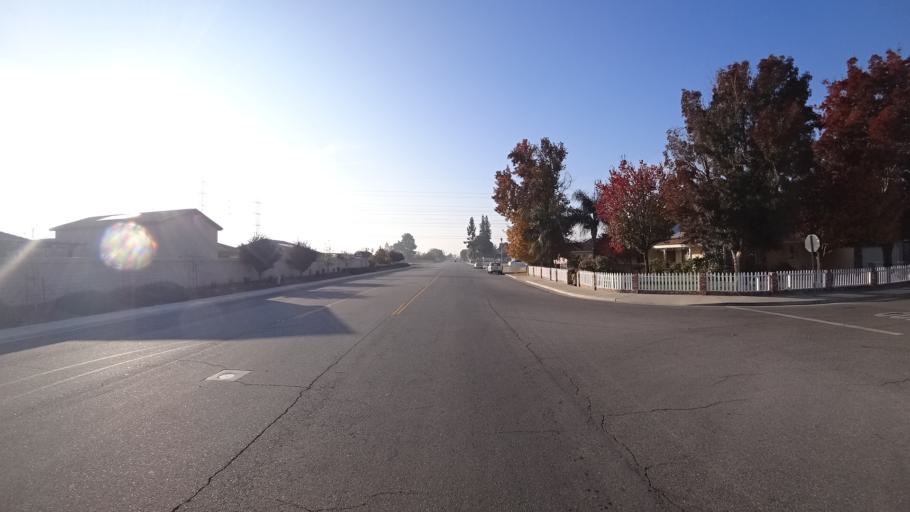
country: US
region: California
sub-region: Kern County
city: Greenacres
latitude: 35.3883
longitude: -119.1190
